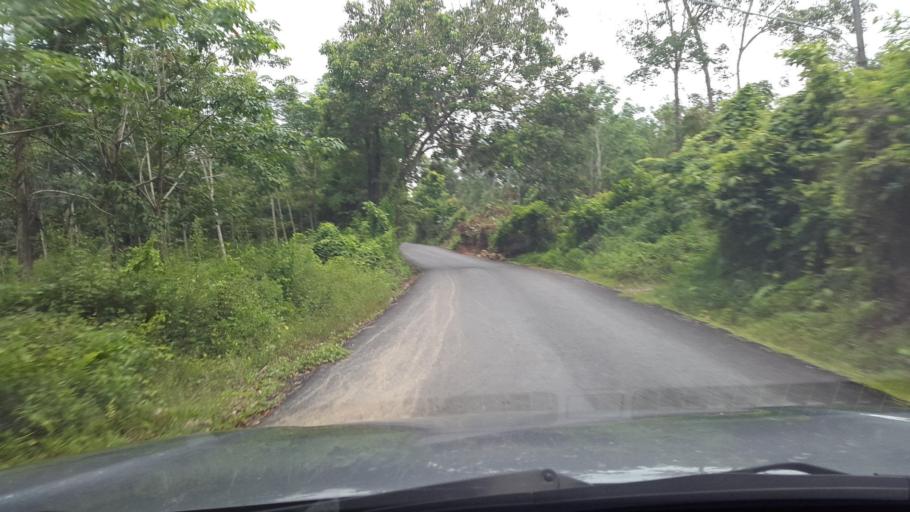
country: ID
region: South Sumatra
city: Sekayu
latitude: -3.0981
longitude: 103.8130
